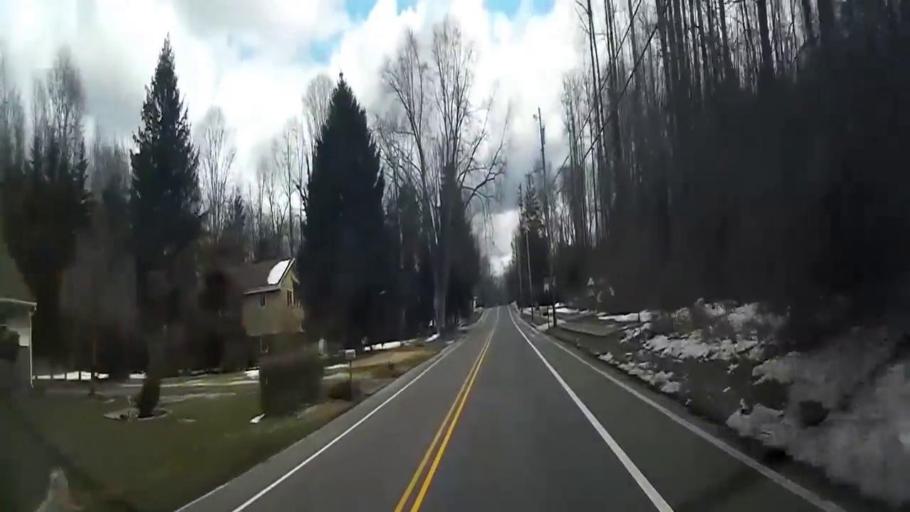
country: US
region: New Jersey
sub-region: Burlington County
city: Marlton
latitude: 39.8579
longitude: -74.9261
